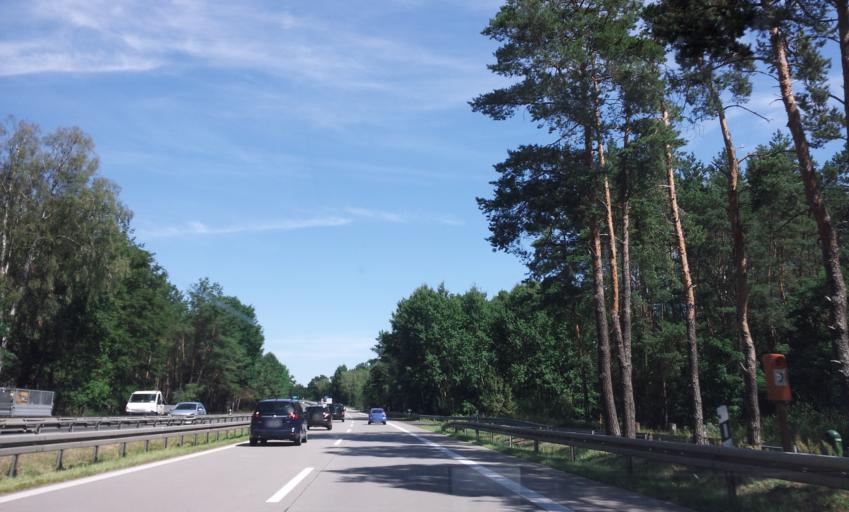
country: DE
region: Brandenburg
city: Marienwerder
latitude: 52.8334
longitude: 13.6601
